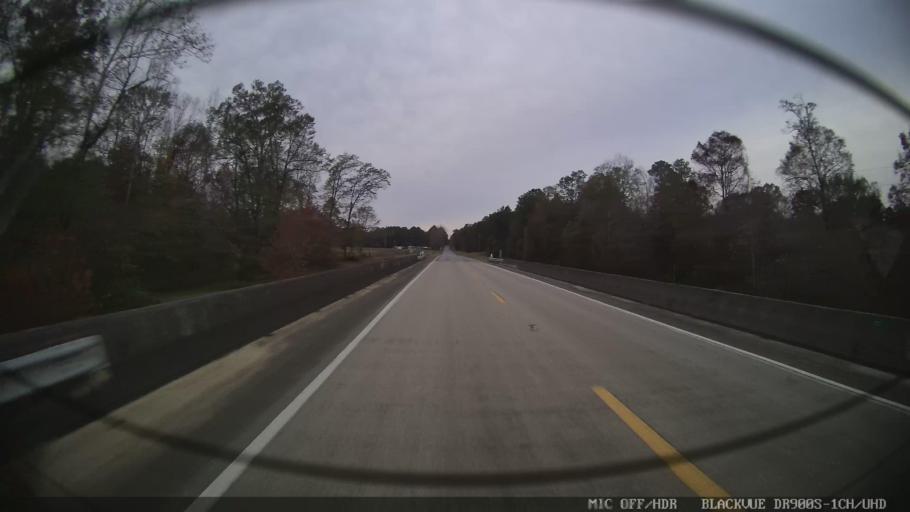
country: US
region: Mississippi
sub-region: Clarke County
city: Quitman
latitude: 32.0289
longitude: -88.8046
